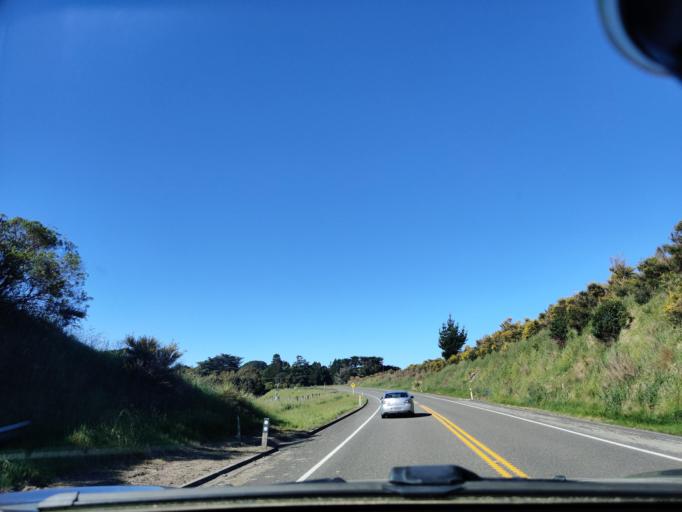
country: NZ
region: Wellington
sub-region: Masterton District
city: Masterton
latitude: -40.6731
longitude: 175.6988
